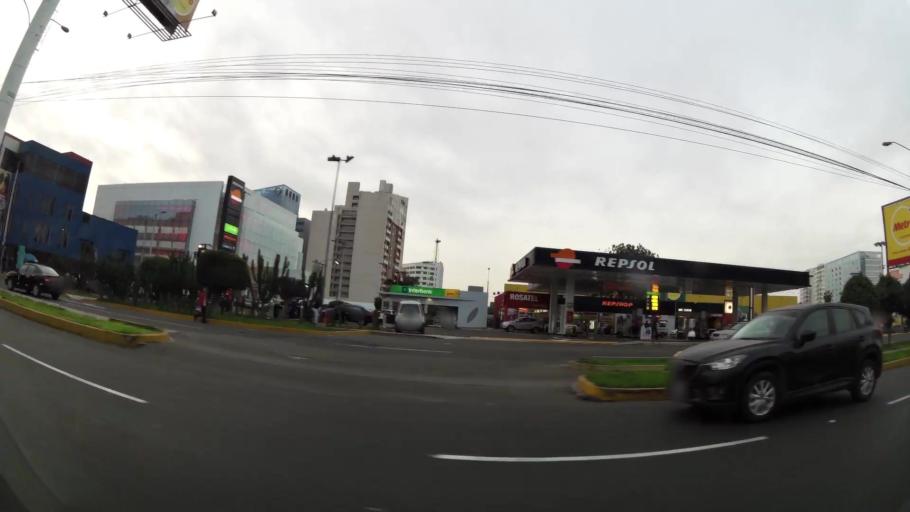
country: PE
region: Callao
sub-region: Callao
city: Callao
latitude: -12.0779
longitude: -77.0900
